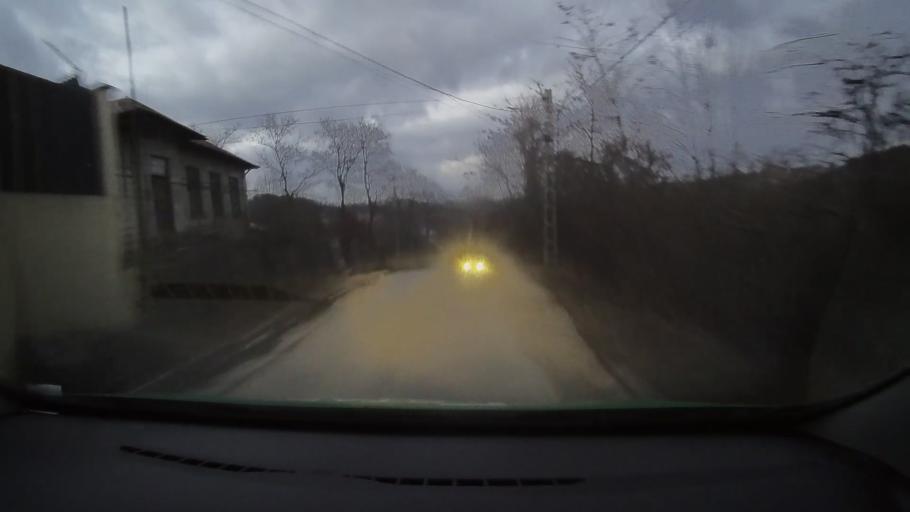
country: RO
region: Prahova
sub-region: Comuna Adunati
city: Adunati
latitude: 45.1367
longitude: 25.6240
